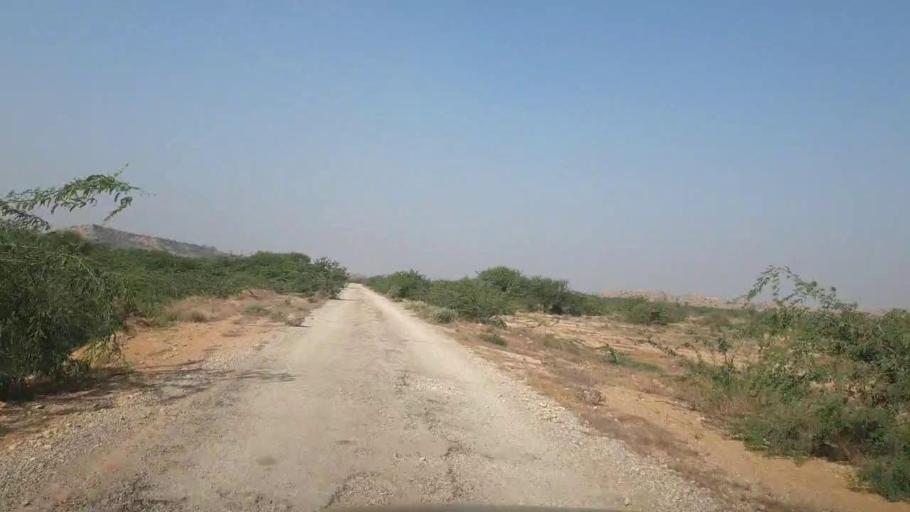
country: PK
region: Sindh
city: Gharo
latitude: 25.0517
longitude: 67.5549
